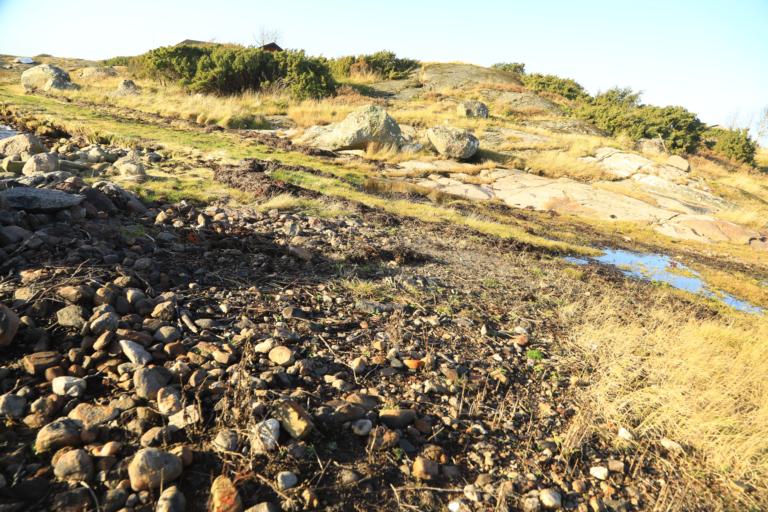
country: SE
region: Halland
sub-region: Varbergs Kommun
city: Varberg
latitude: 57.1627
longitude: 12.2190
